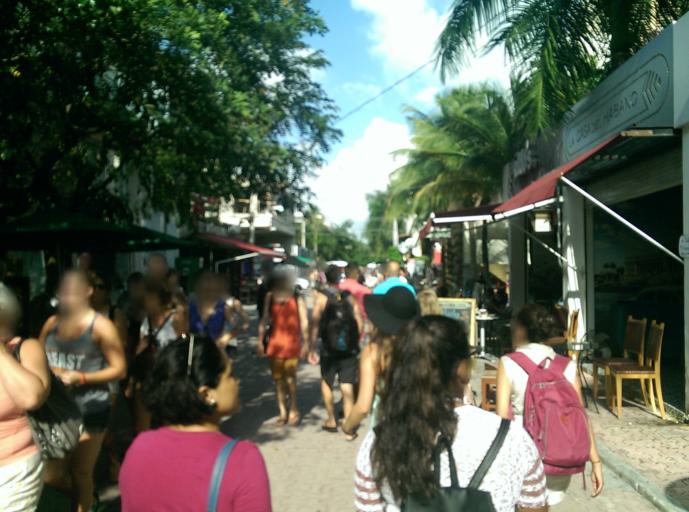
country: MX
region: Quintana Roo
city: Playa del Carmen
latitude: 20.6322
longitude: -87.0683
